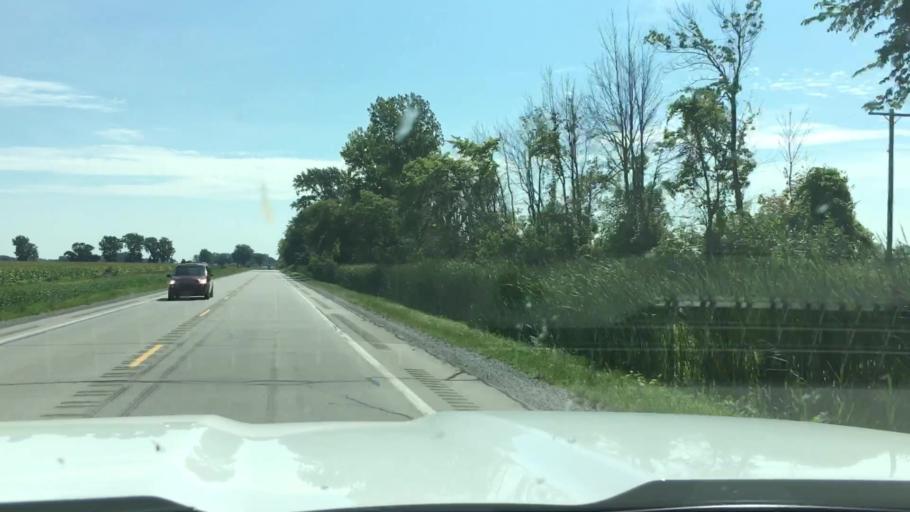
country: US
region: Michigan
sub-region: Bay County
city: Essexville
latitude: 43.5840
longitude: -83.7140
